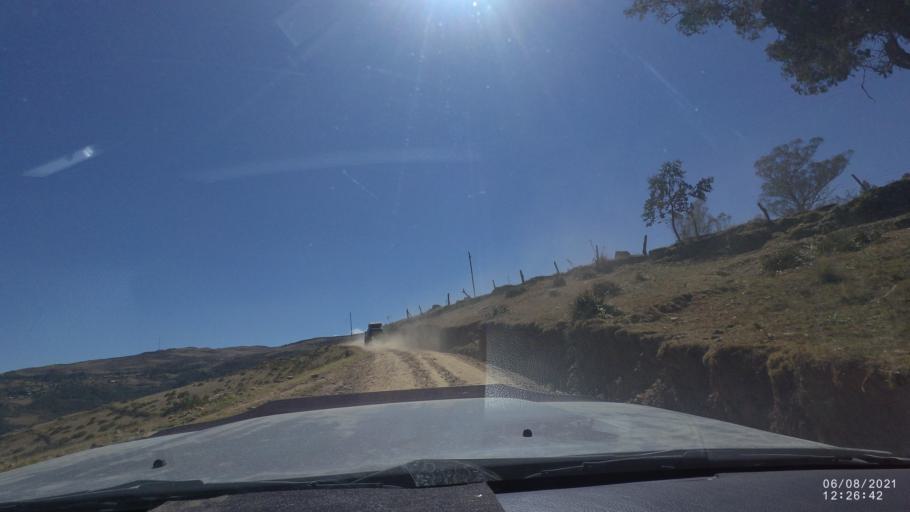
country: BO
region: Cochabamba
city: Colchani
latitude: -16.7920
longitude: -66.6549
